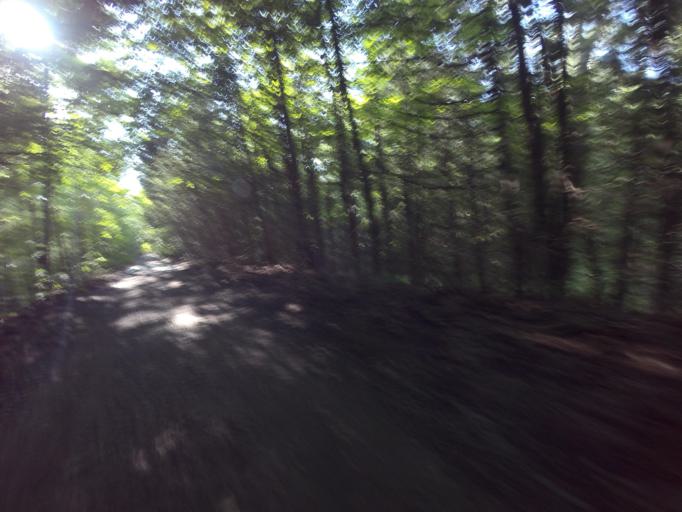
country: CA
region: Ontario
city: Goderich
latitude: 43.7533
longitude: -81.5705
